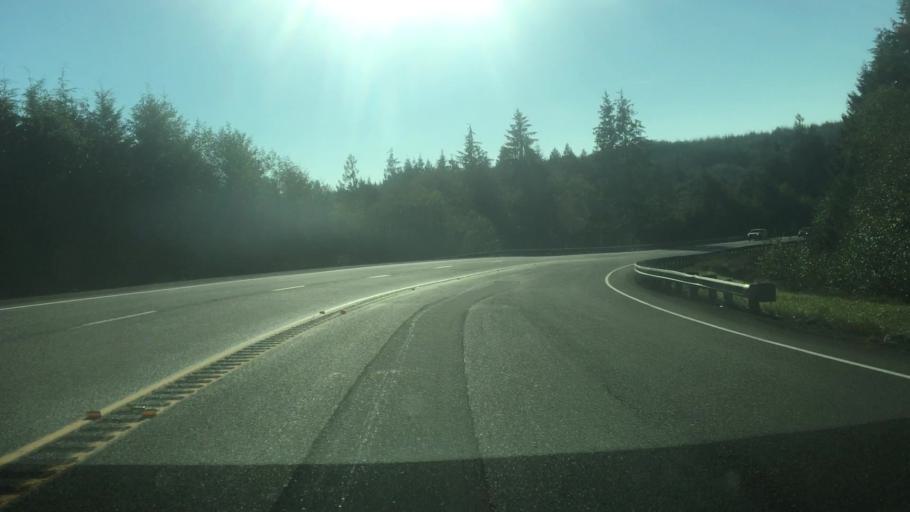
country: US
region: Washington
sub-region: Pacific County
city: South Bend
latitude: 46.6802
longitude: -123.8940
